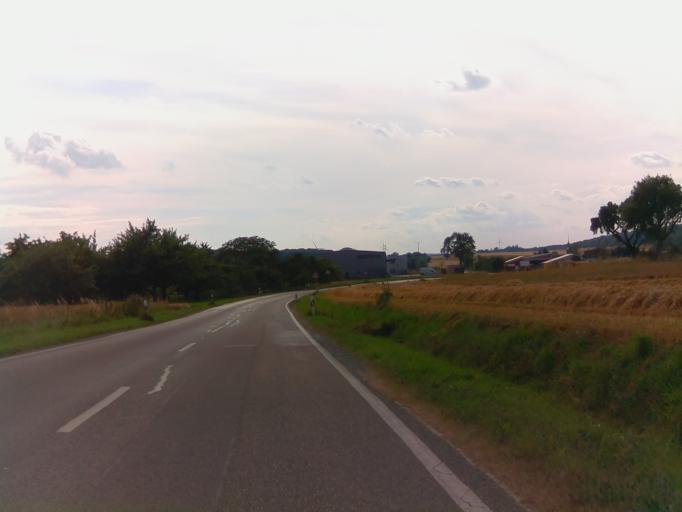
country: DE
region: Baden-Wuerttemberg
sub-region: Regierungsbezirk Stuttgart
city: Buch am Ahorn
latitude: 49.5377
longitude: 9.5680
